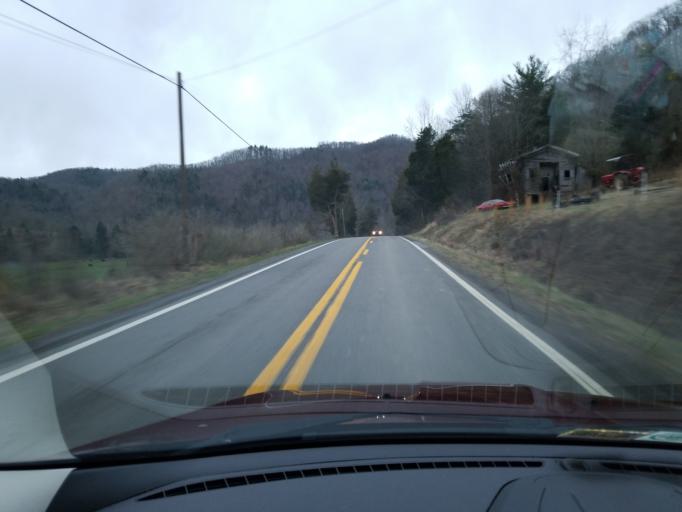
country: US
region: West Virginia
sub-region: Monroe County
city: Union
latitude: 37.5317
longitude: -80.6010
